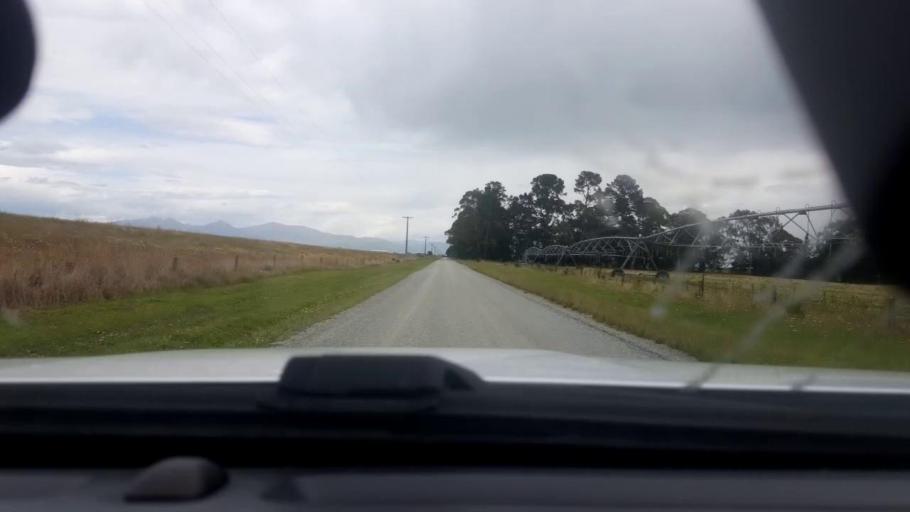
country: NZ
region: Canterbury
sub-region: Timaru District
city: Pleasant Point
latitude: -44.1526
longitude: 171.3962
